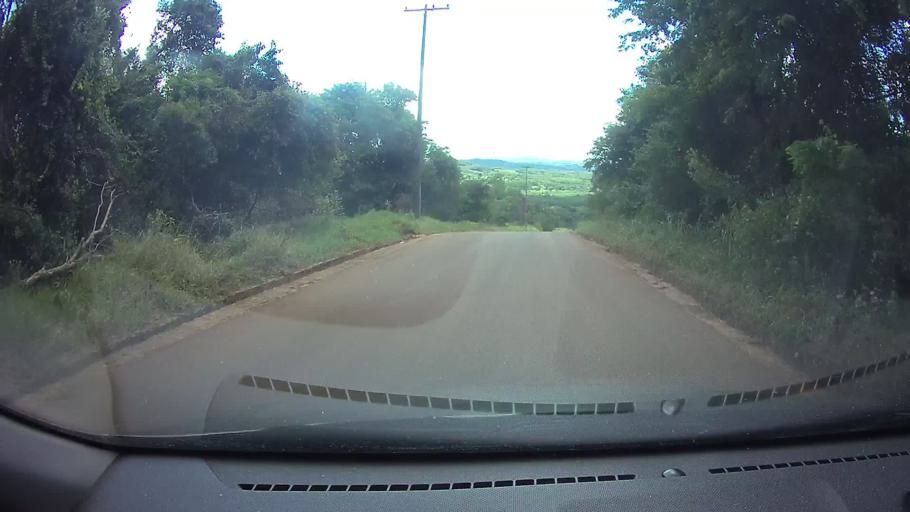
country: PY
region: Paraguari
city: La Colmena
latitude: -25.9291
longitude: -56.7865
